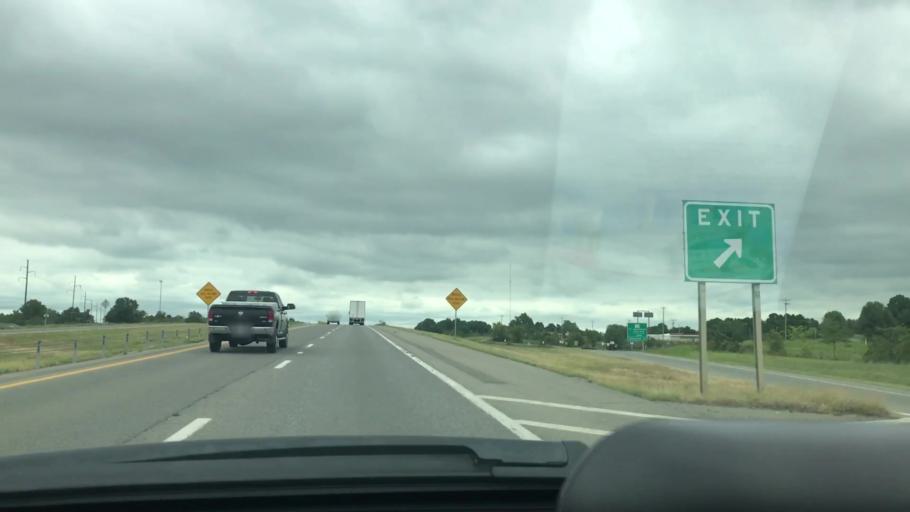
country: US
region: Oklahoma
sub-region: McIntosh County
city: Eufaula
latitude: 35.3598
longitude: -95.5747
